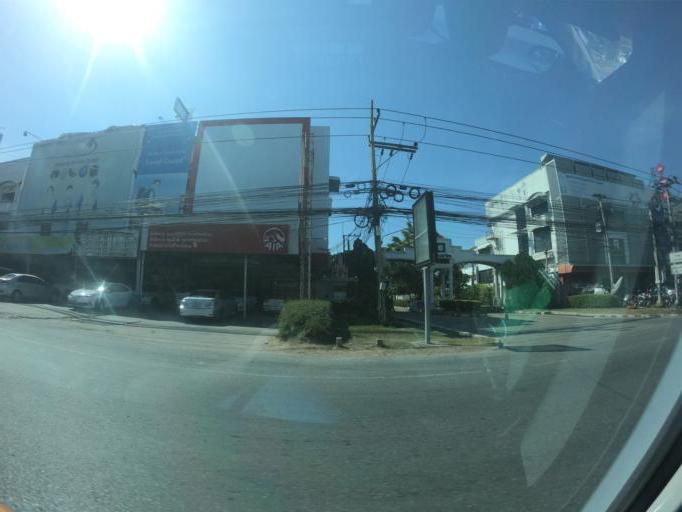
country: TH
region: Khon Kaen
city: Khon Kaen
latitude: 16.4034
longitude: 102.8324
